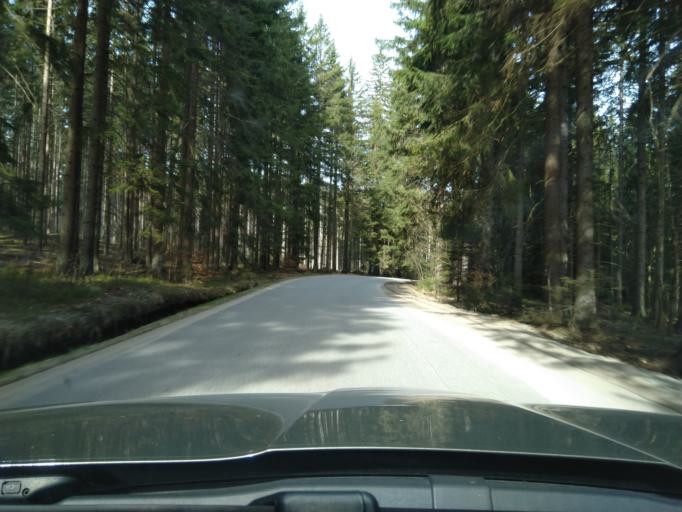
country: CZ
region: Jihocesky
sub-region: Okres Prachatice
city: Stachy
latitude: 49.0647
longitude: 13.6528
